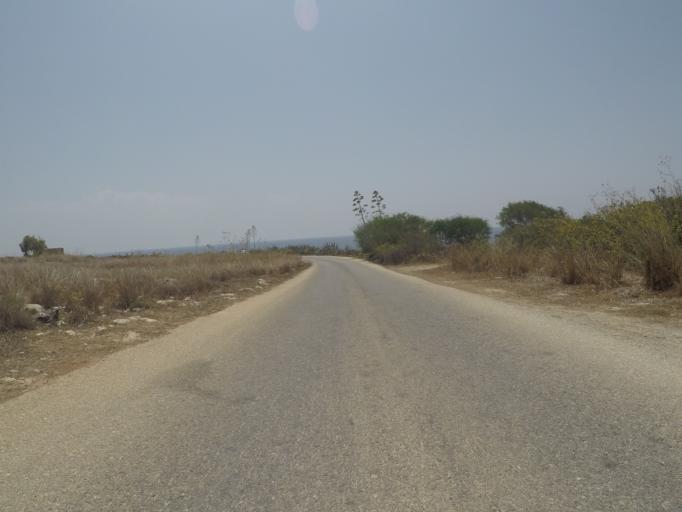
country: MT
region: Is-Siggiewi
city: Siggiewi
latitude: 35.8299
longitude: 14.4206
